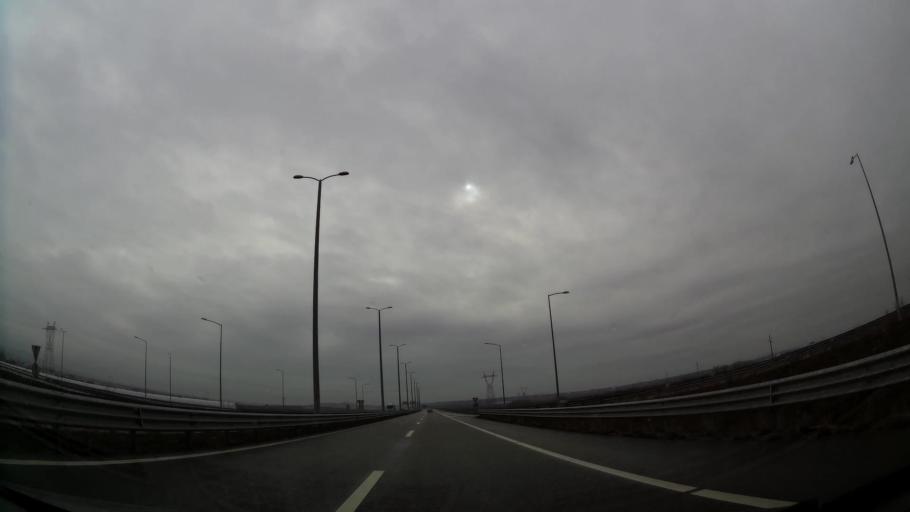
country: XK
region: Pristina
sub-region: Lipjan
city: Lipljan
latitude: 42.4620
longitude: 21.1790
